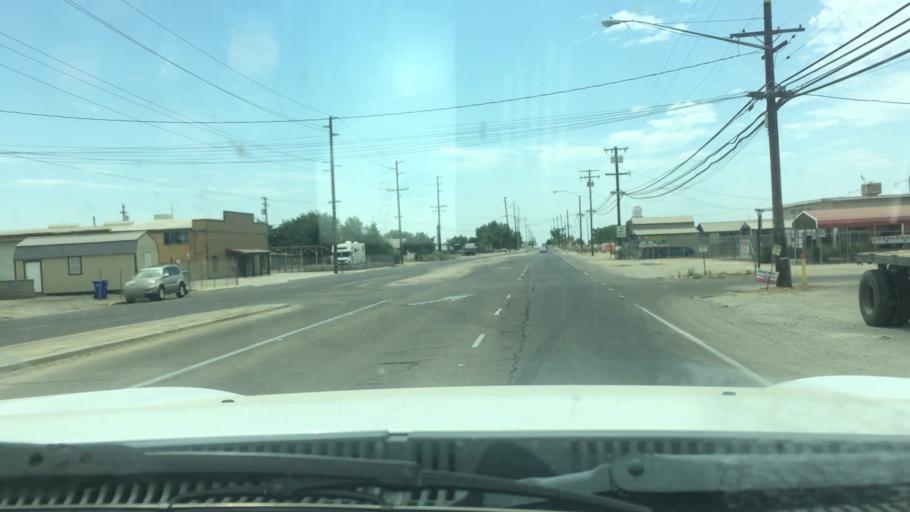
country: US
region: California
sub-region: Tulare County
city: Porterville
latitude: 36.0659
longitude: -119.0749
